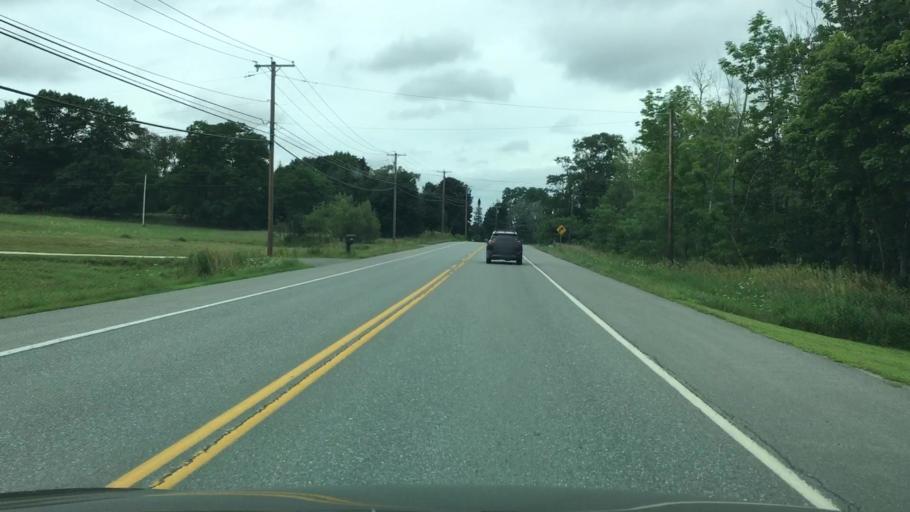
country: US
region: Maine
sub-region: Penobscot County
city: Orrington
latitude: 44.7131
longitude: -68.8266
